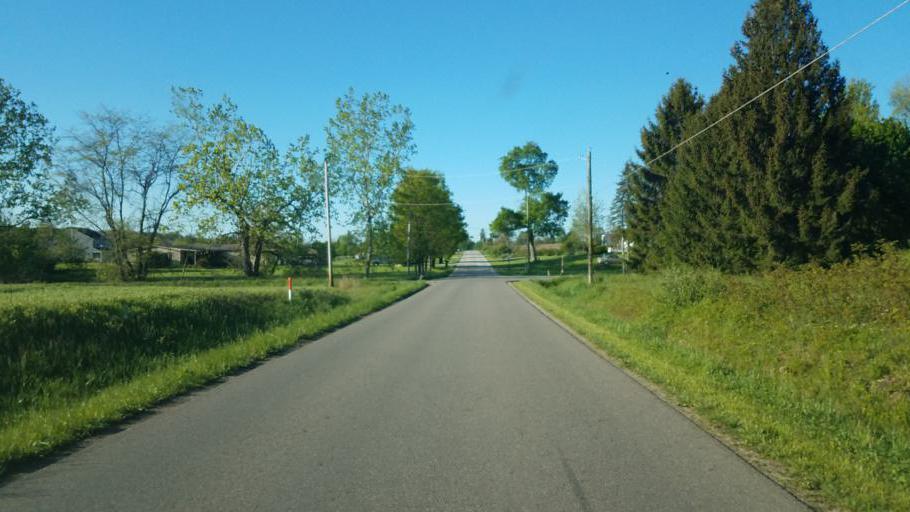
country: US
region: Ohio
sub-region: Morrow County
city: Cardington
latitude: 40.3868
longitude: -82.8138
